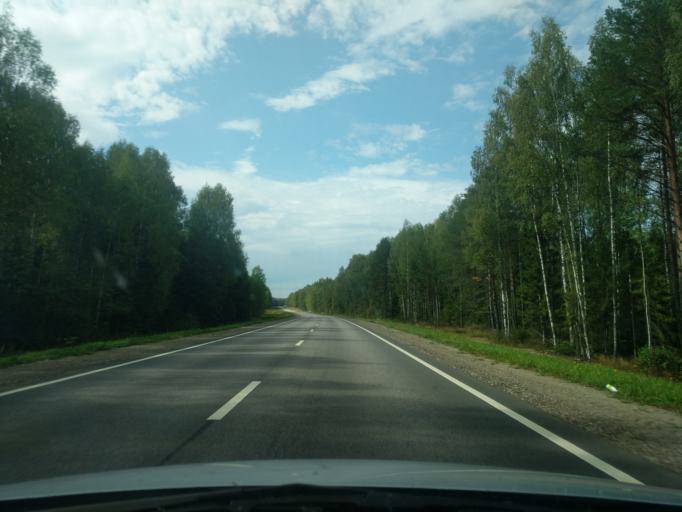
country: RU
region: Kostroma
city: Kadyy
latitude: 57.7981
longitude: 42.8741
